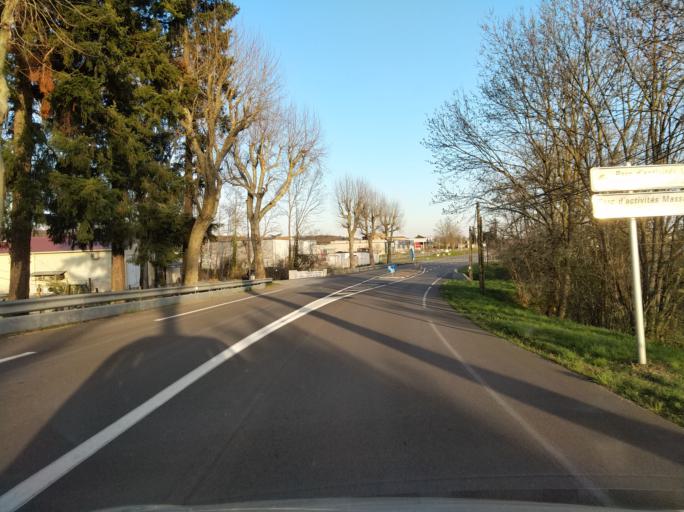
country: FR
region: Rhone-Alpes
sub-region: Departement de l'Ardeche
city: Boulieu-les-Annonay
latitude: 45.2695
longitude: 4.6791
